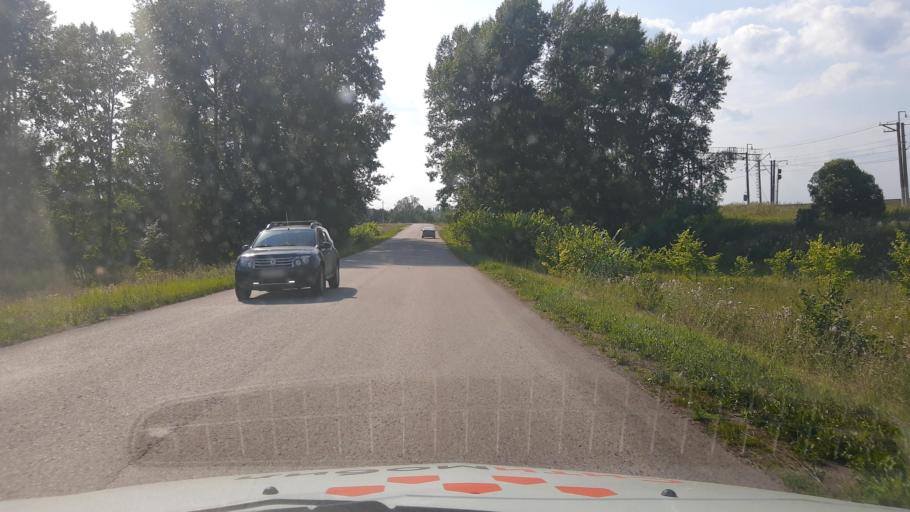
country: RU
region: Bashkortostan
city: Kabakovo
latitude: 54.6623
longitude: 56.1822
